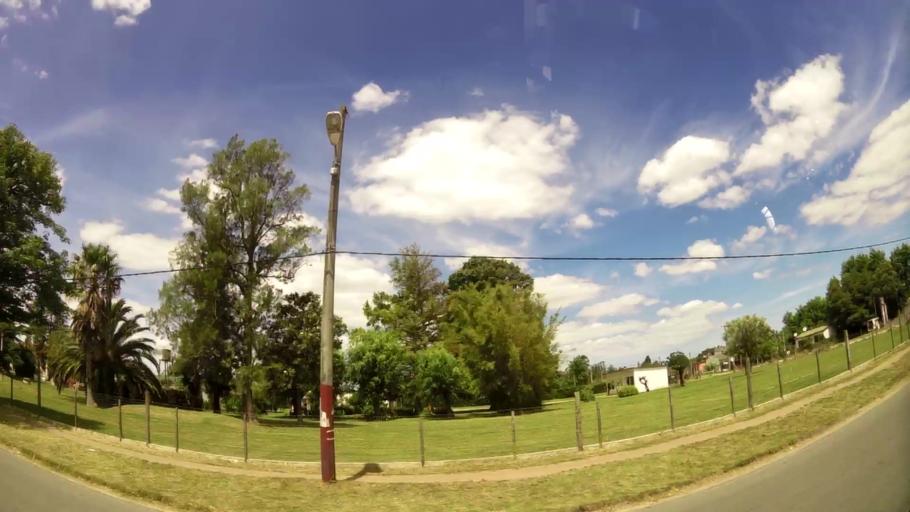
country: UY
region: San Jose
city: Delta del Tigre
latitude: -34.7453
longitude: -56.4526
